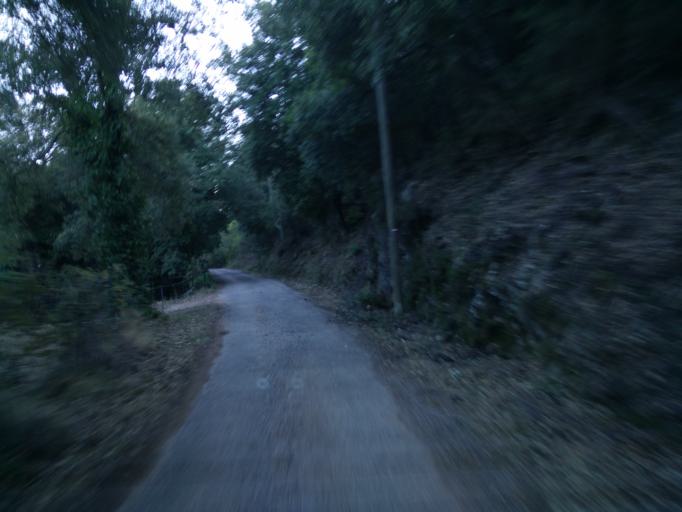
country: FR
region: Provence-Alpes-Cote d'Azur
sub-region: Departement du Var
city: Collobrieres
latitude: 43.2589
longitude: 6.3048
